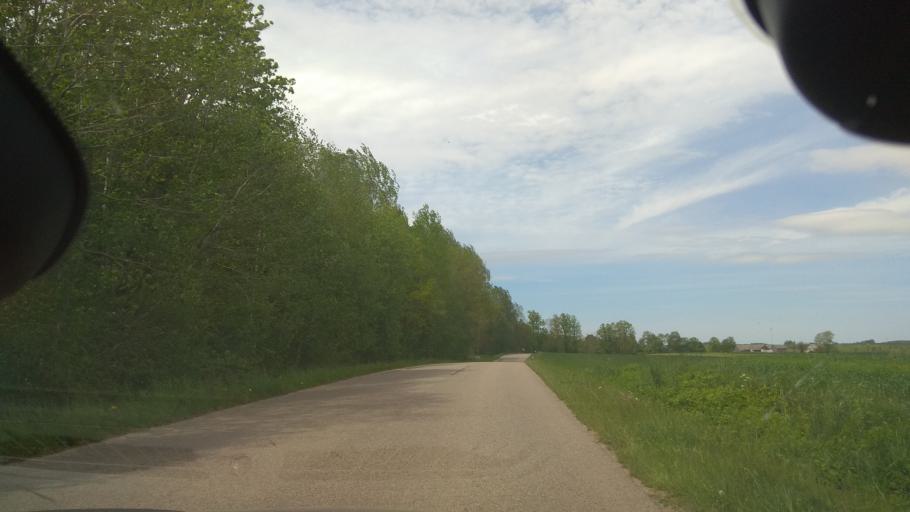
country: LT
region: Vilnius County
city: Ukmerge
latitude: 55.1520
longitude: 24.5480
